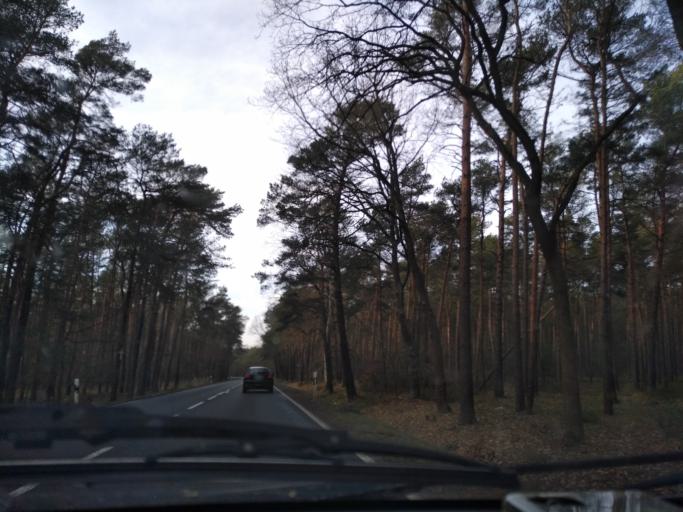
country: DE
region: Brandenburg
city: Herzberg
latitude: 51.7238
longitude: 13.2284
